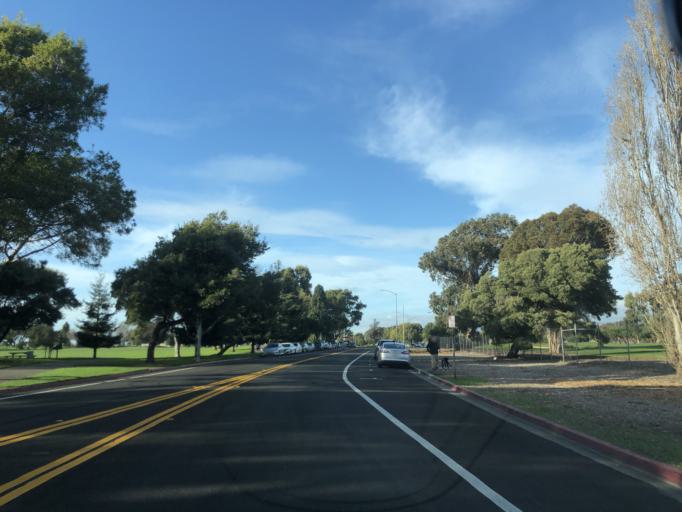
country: US
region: California
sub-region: Alameda County
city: San Leandro
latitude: 37.6922
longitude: -122.1844
